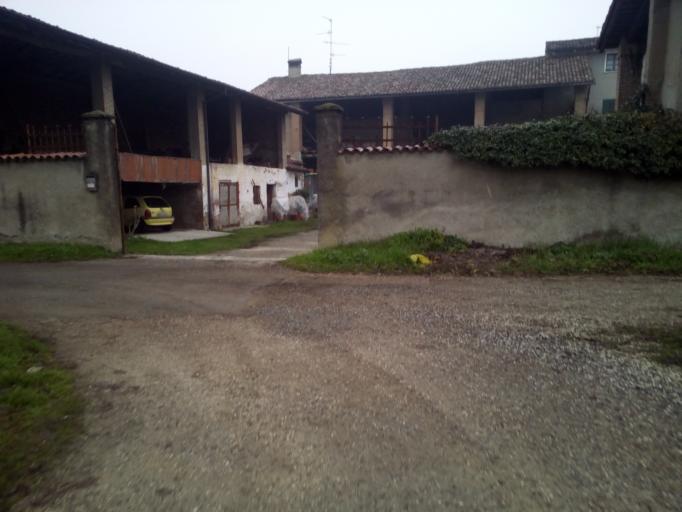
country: IT
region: Lombardy
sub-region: Provincia di Brescia
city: Castel Mella
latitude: 45.5093
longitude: 10.1512
